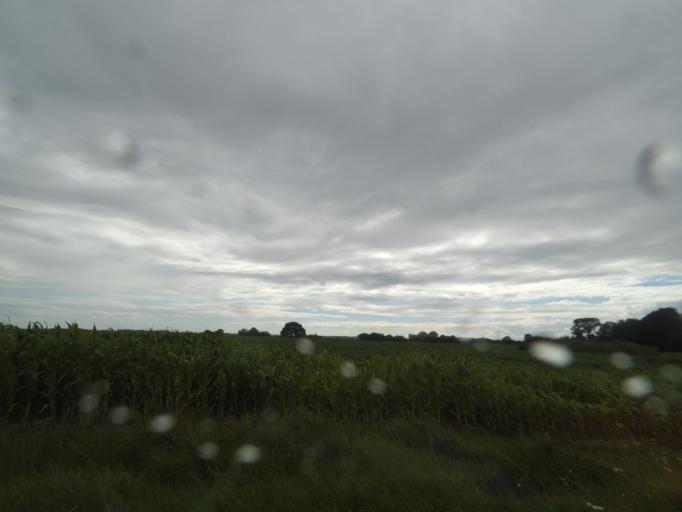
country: DK
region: South Denmark
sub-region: Nordfyns Kommune
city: Sonderso
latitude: 55.4898
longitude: 10.2379
